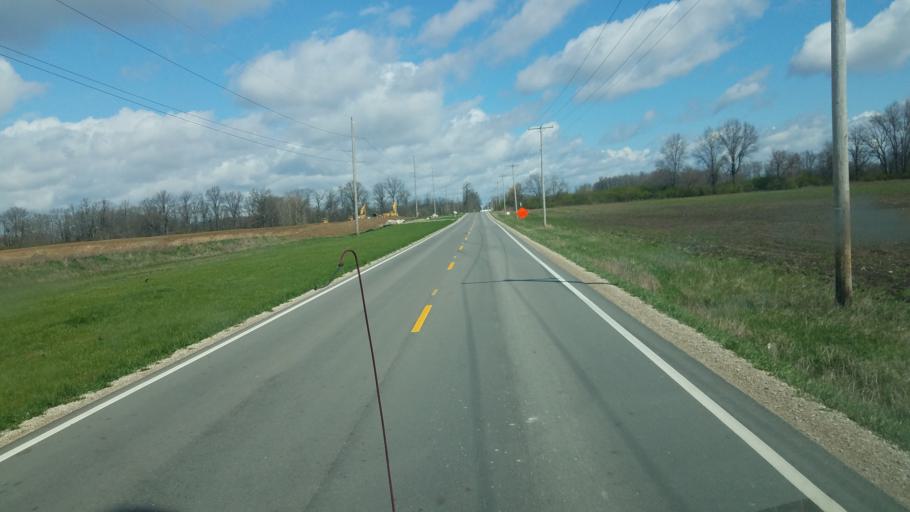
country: US
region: Ohio
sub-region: Delaware County
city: Delaware
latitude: 40.2910
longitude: -83.1275
